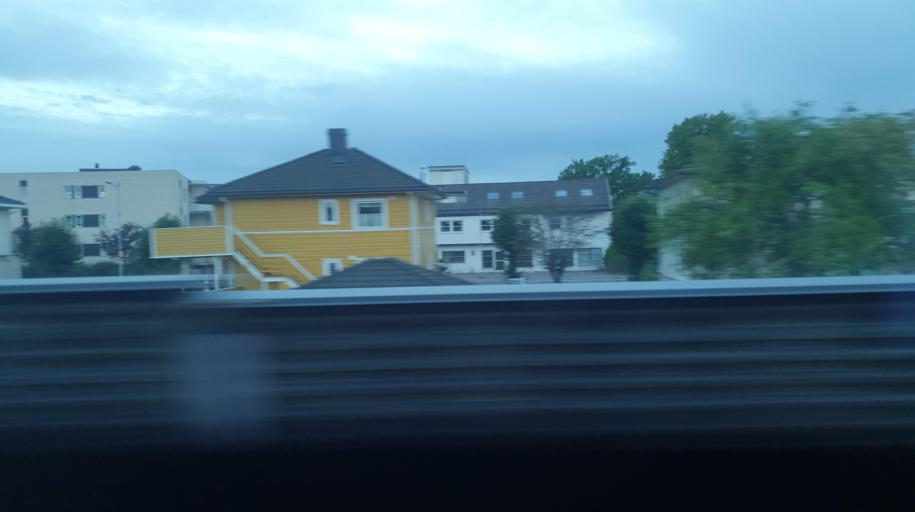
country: NO
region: Vestfold
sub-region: Tonsberg
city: Tonsberg
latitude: 59.2767
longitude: 10.4075
